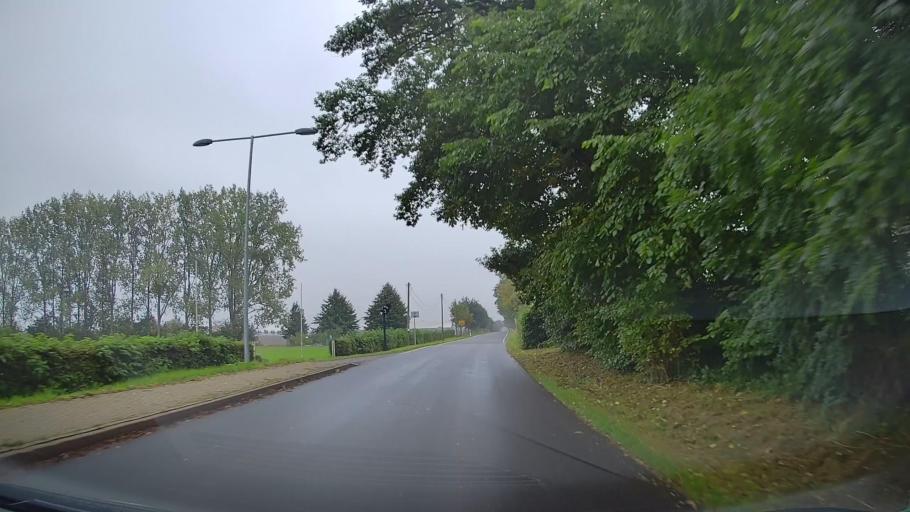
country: DE
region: Mecklenburg-Vorpommern
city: Gramkow
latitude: 53.9240
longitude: 11.3782
